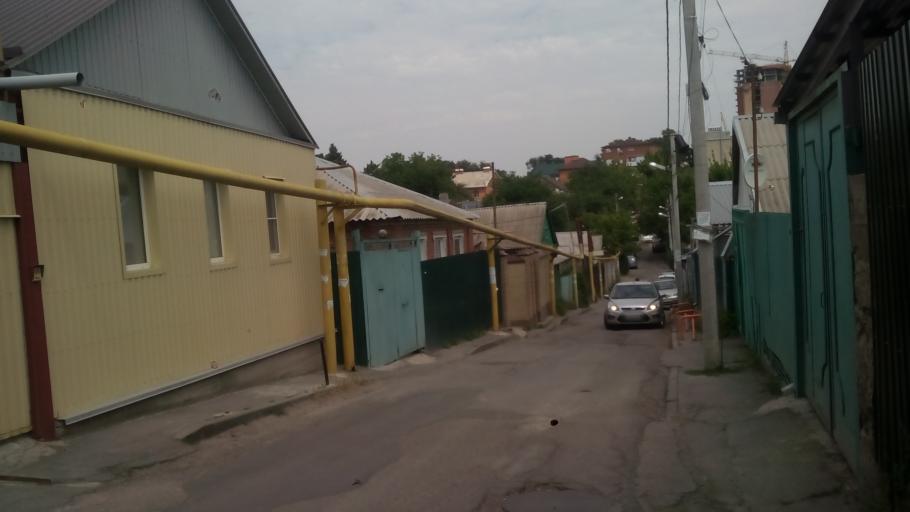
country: RU
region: Rostov
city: Rostov-na-Donu
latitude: 47.2464
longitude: 39.7427
